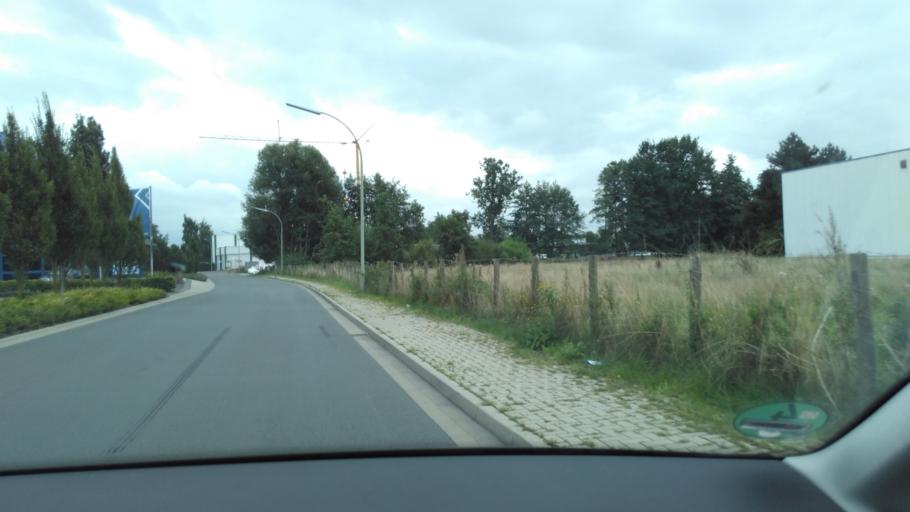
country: DE
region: North Rhine-Westphalia
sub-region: Regierungsbezirk Detmold
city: Verl
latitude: 51.8715
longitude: 8.4620
